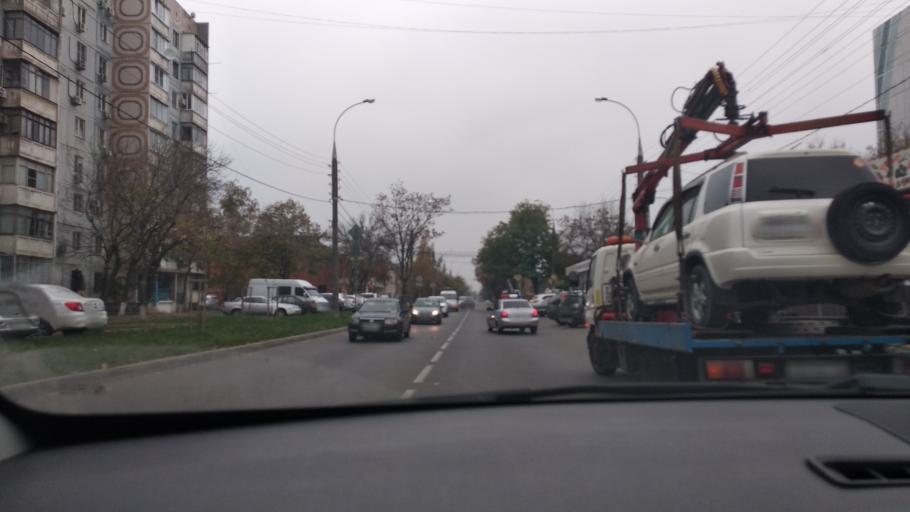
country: RU
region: Krasnodarskiy
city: Krasnodar
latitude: 45.0205
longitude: 39.0100
